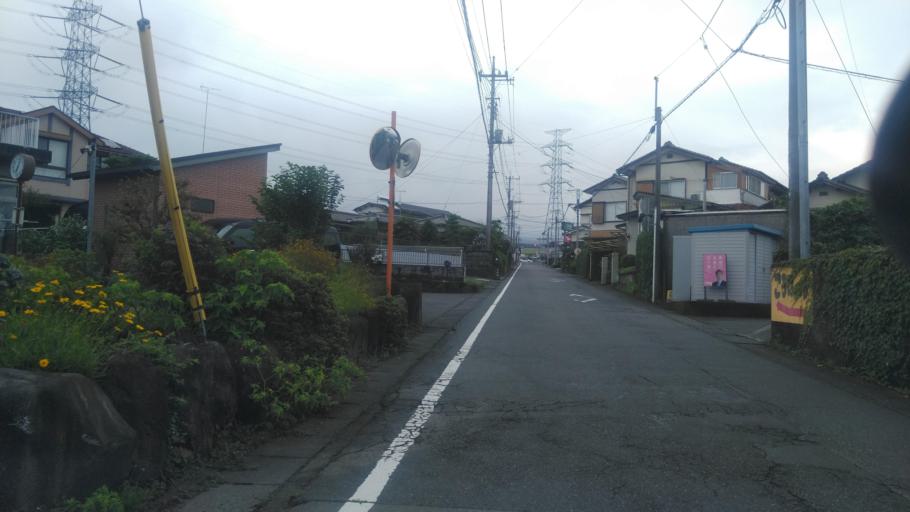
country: JP
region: Shizuoka
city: Fujinomiya
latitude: 35.2548
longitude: 138.6143
